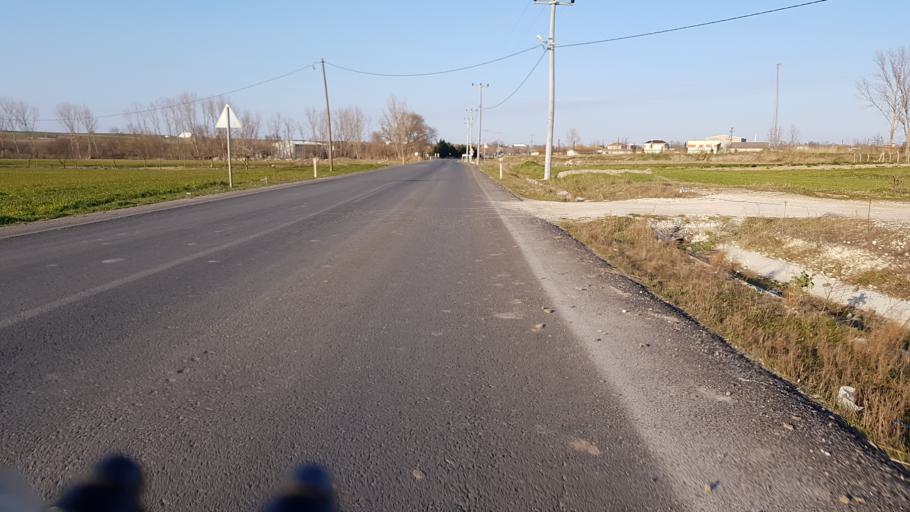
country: TR
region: Tekirdag
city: Beyazkoy
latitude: 41.2971
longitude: 27.7764
